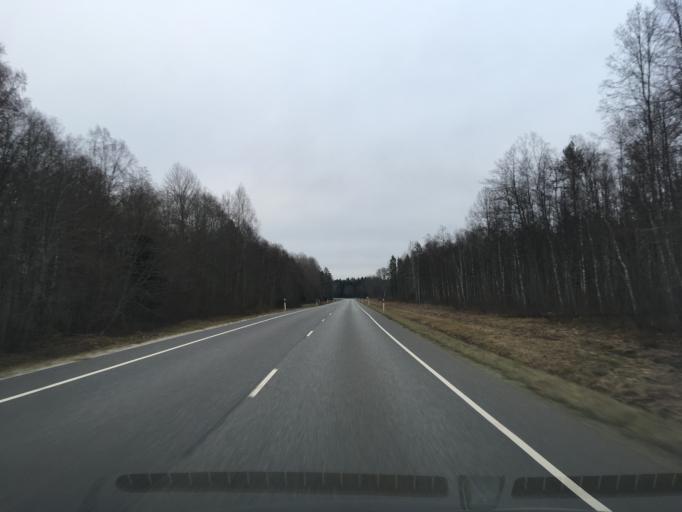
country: EE
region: Laeaene-Virumaa
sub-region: Kadrina vald
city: Kadrina
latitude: 59.4496
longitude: 26.0553
